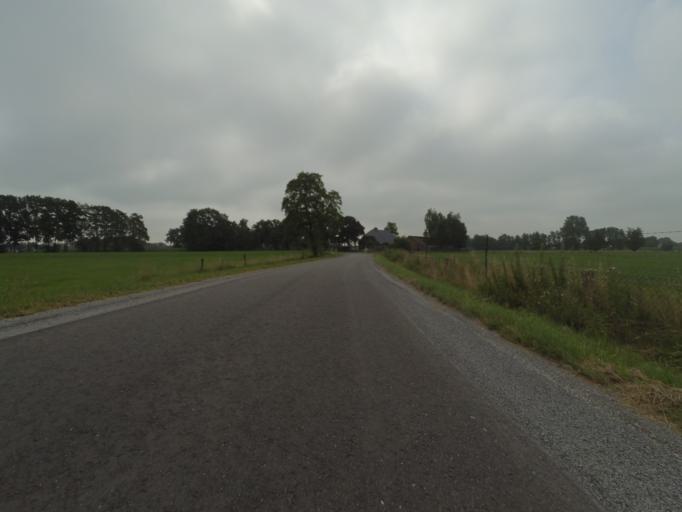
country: NL
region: Gelderland
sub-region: Gemeente Barneveld
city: Barneveld
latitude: 52.1388
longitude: 5.6169
